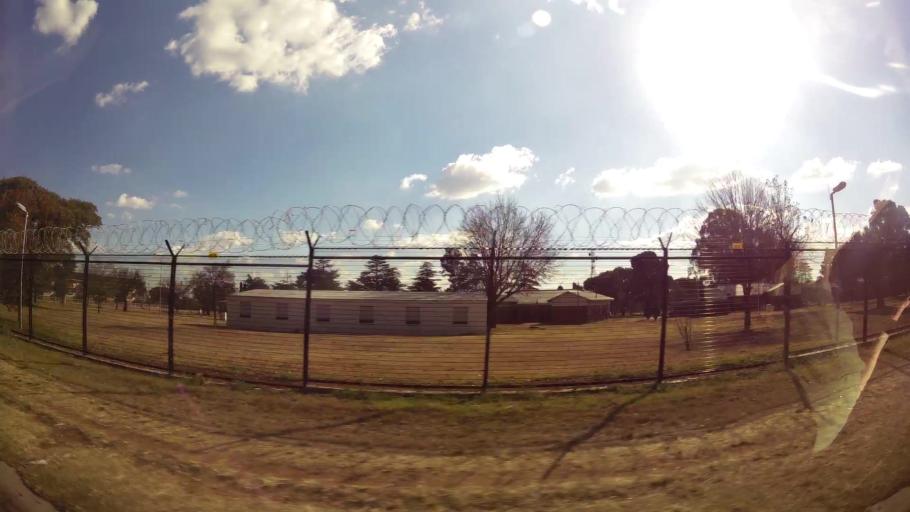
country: ZA
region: Mpumalanga
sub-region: Nkangala District Municipality
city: Witbank
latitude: -25.8892
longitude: 29.2211
